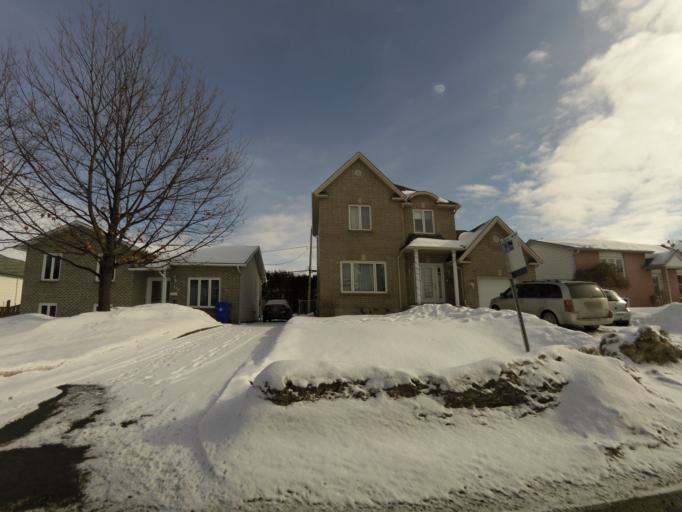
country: CA
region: Quebec
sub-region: Outaouais
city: Gatineau
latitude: 45.4979
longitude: -75.5806
